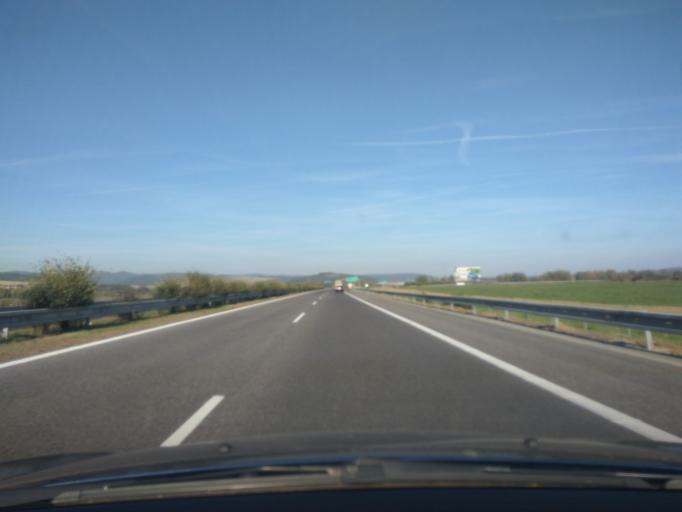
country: SK
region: Trenciansky
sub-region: Okres Trencin
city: Trencin
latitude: 48.8522
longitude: 17.9498
